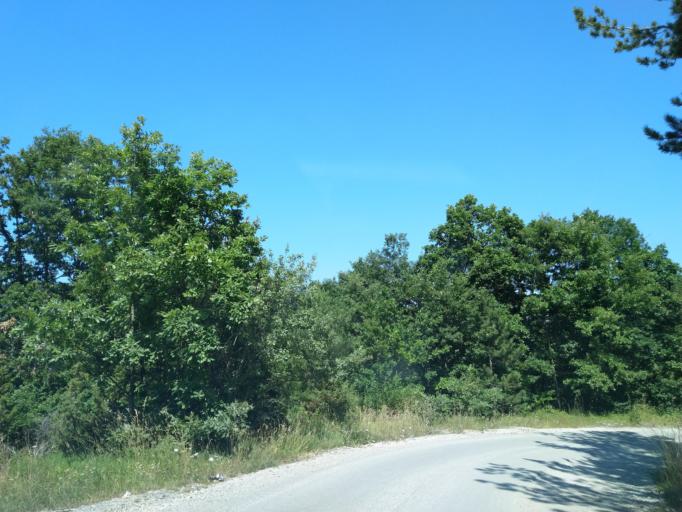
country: RS
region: Central Serbia
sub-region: Zlatiborski Okrug
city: Uzice
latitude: 43.8040
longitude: 19.8159
